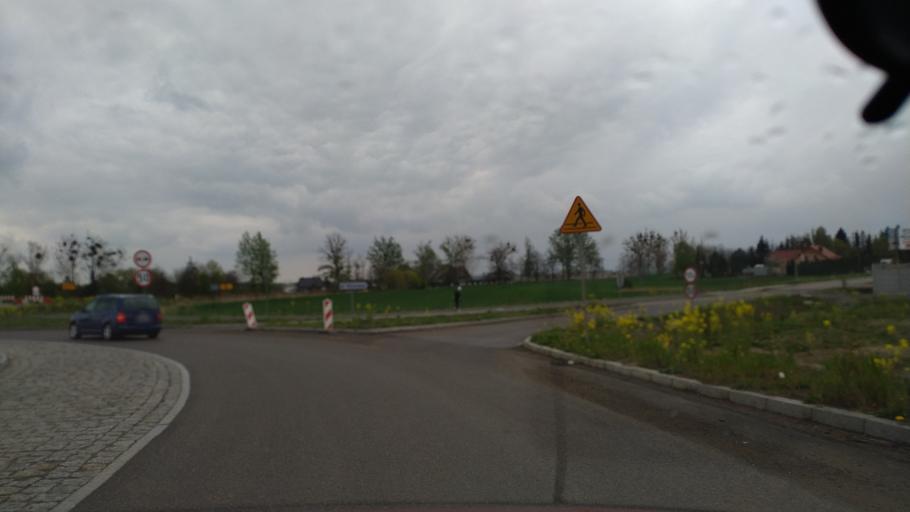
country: PL
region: Pomeranian Voivodeship
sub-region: Powiat tczewski
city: Subkowy
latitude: 54.0481
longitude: 18.7577
